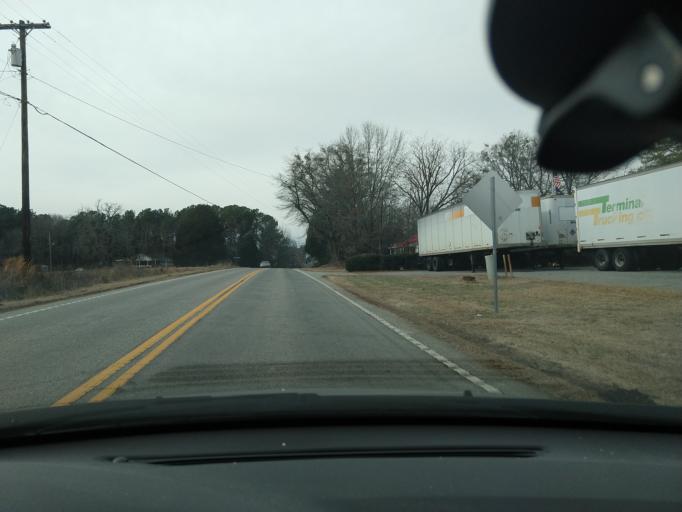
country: US
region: South Carolina
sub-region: Spartanburg County
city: Cowpens
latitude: 35.0089
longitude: -81.8550
